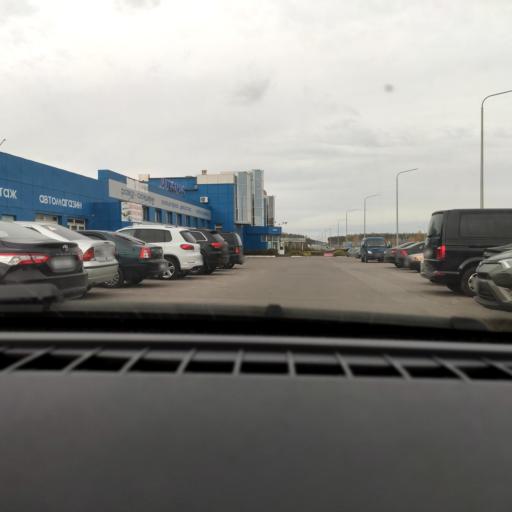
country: RU
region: Voronezj
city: Somovo
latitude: 51.6808
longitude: 39.3013
